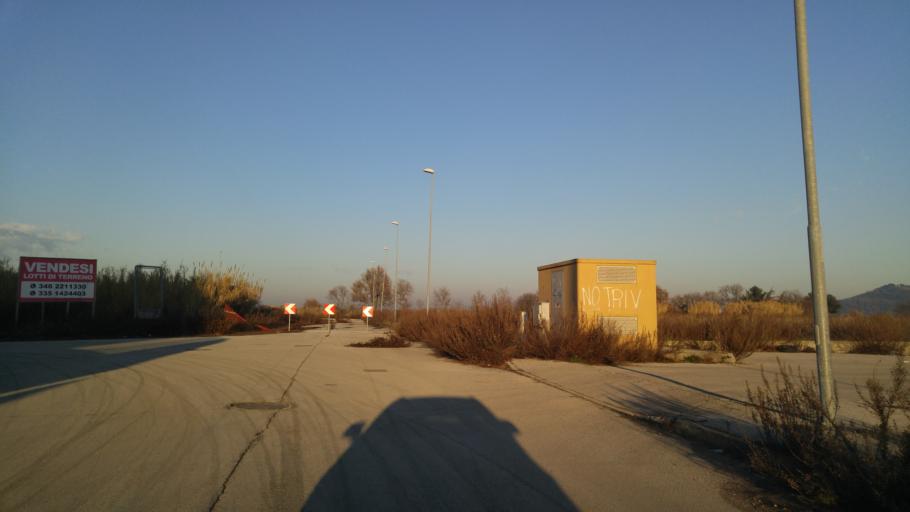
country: IT
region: The Marches
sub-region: Provincia di Ancona
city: Monterado
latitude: 43.7108
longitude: 13.0805
